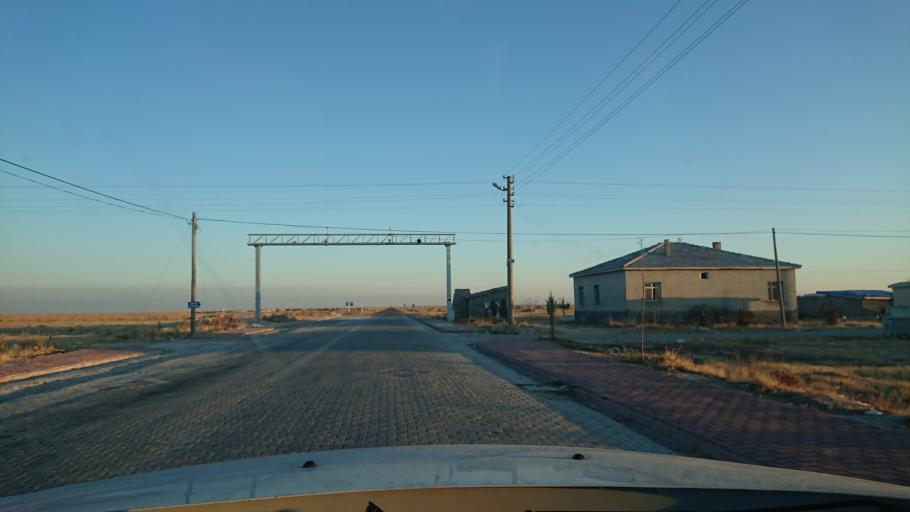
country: TR
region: Aksaray
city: Eskil
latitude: 38.3936
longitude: 33.4261
